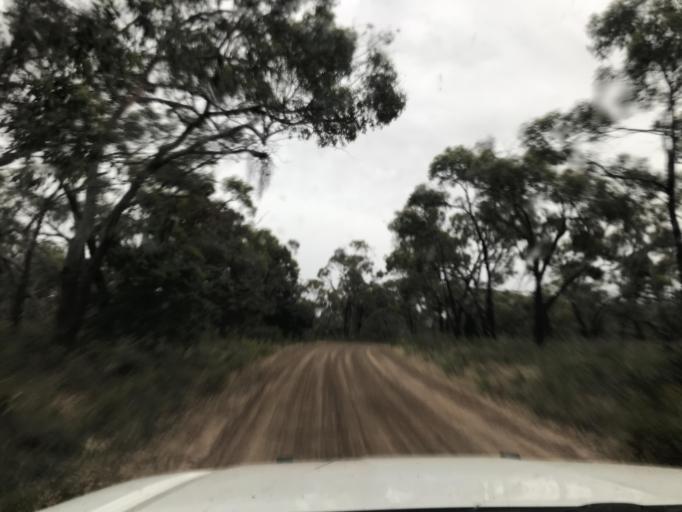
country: AU
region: South Australia
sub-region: Wattle Range
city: Penola
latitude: -37.0932
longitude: 141.5029
